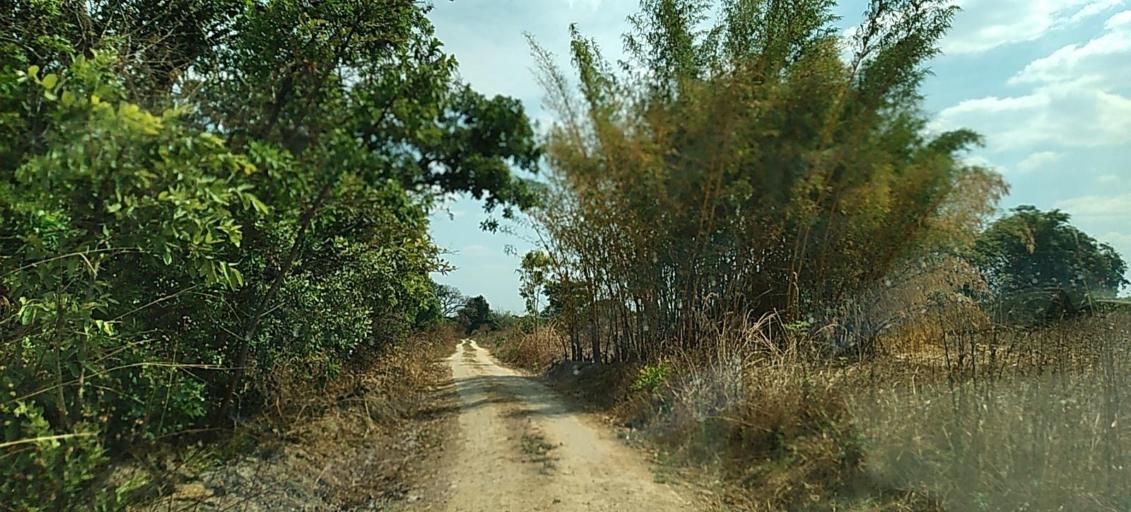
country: ZM
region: Copperbelt
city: Chililabombwe
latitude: -12.3278
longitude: 27.7869
